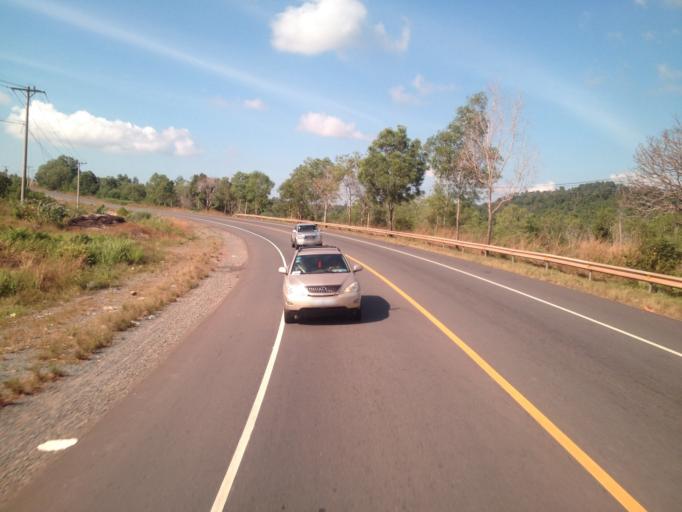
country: KH
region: Preah Sihanouk
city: Sihanoukville
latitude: 10.6066
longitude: 103.6142
